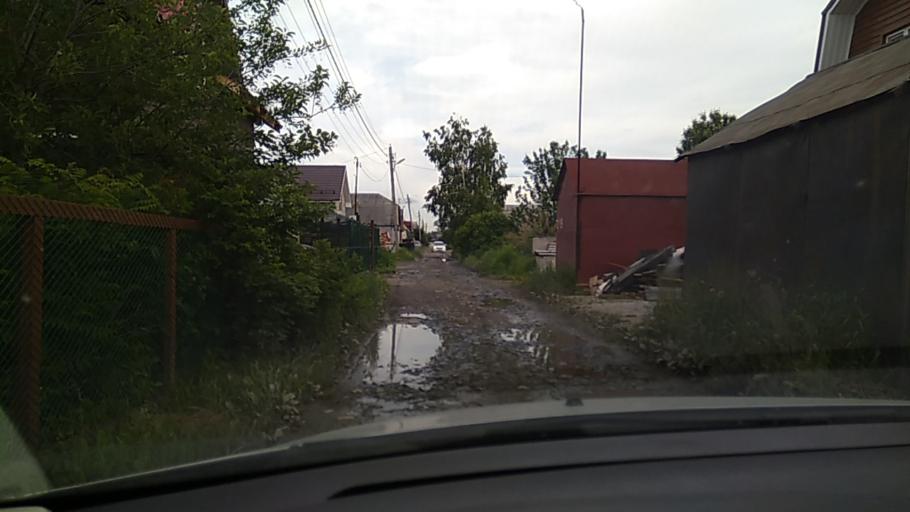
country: RU
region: Sverdlovsk
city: Sredneuralsk
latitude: 56.9716
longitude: 60.4669
